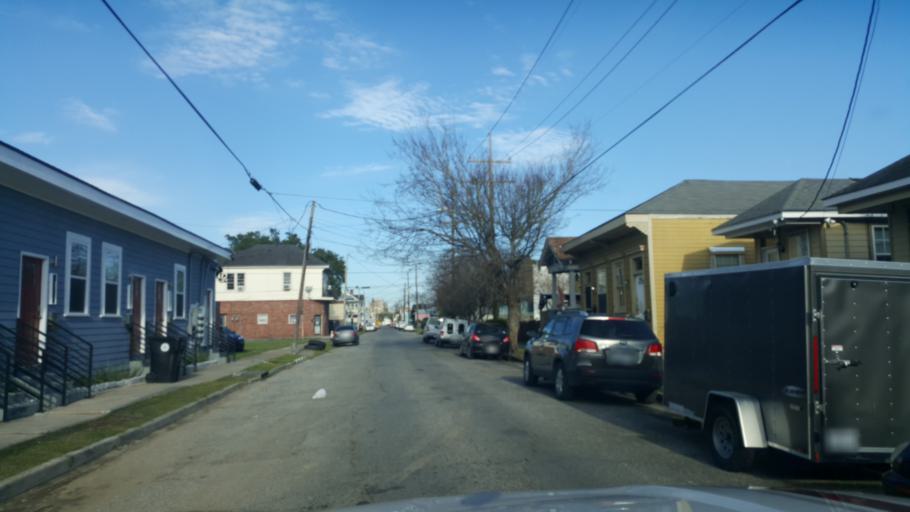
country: US
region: Louisiana
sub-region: Orleans Parish
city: New Orleans
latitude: 29.9324
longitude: -90.0898
